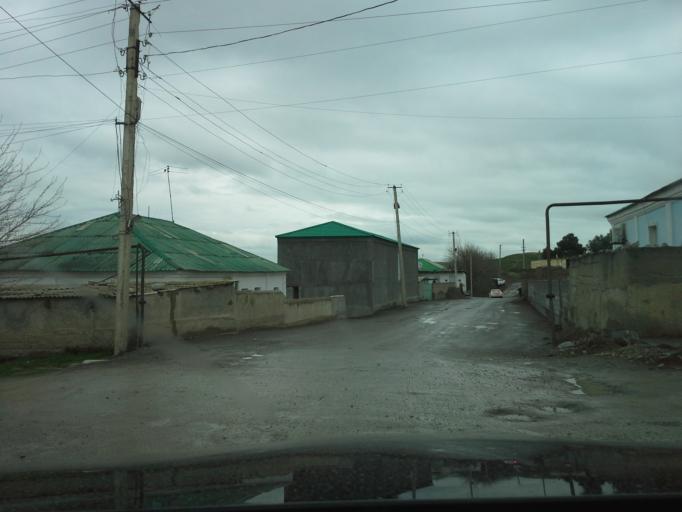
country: TM
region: Ahal
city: Abadan
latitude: 37.9591
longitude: 58.2121
